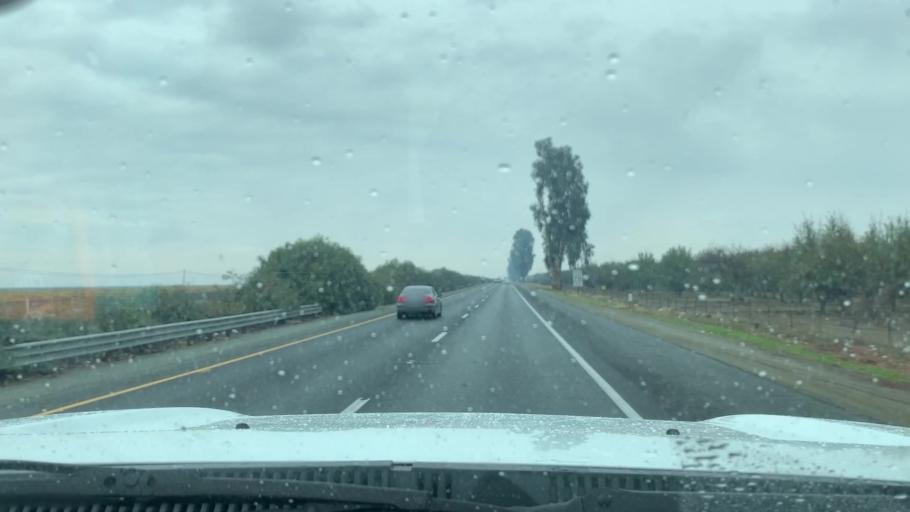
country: US
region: California
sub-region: Kern County
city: Delano
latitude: 35.7975
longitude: -119.2539
